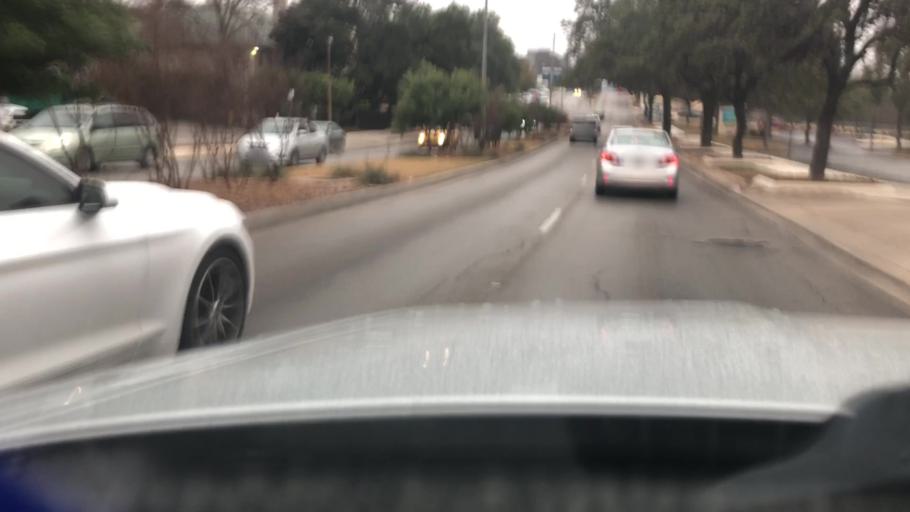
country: US
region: Texas
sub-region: Bexar County
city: Balcones Heights
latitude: 29.5192
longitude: -98.5742
